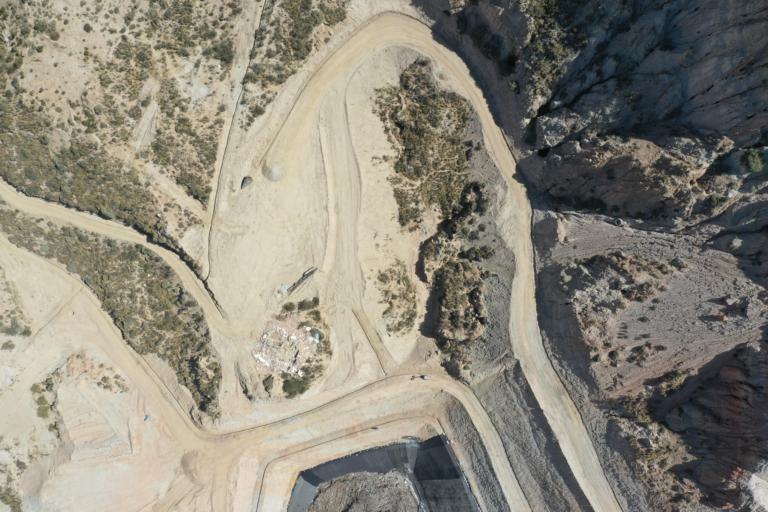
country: BO
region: La Paz
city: La Paz
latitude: -16.5544
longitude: -68.1290
